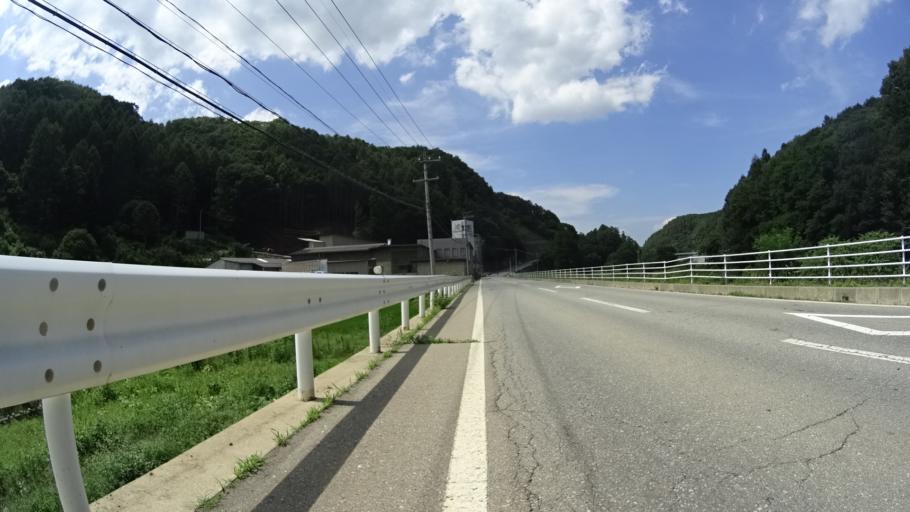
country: JP
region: Nagano
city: Saku
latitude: 36.0747
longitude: 138.4941
